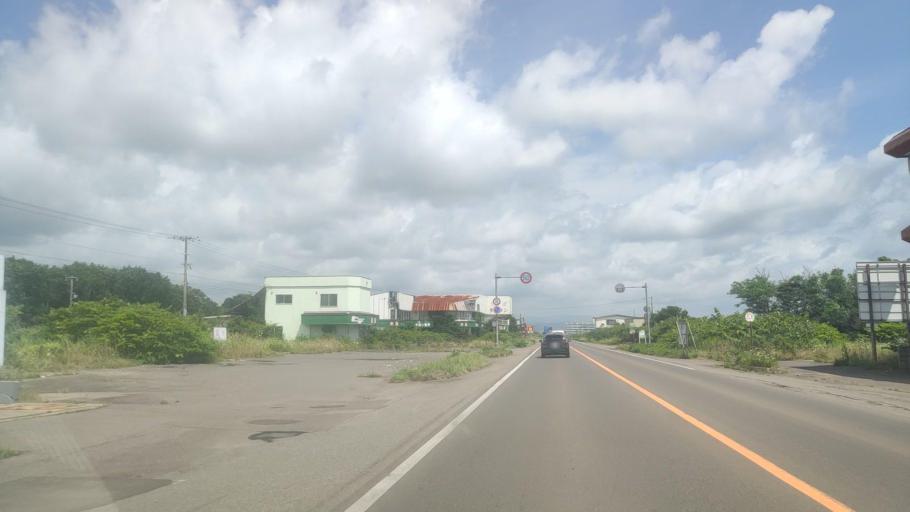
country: JP
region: Hokkaido
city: Niseko Town
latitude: 42.4929
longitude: 140.3600
